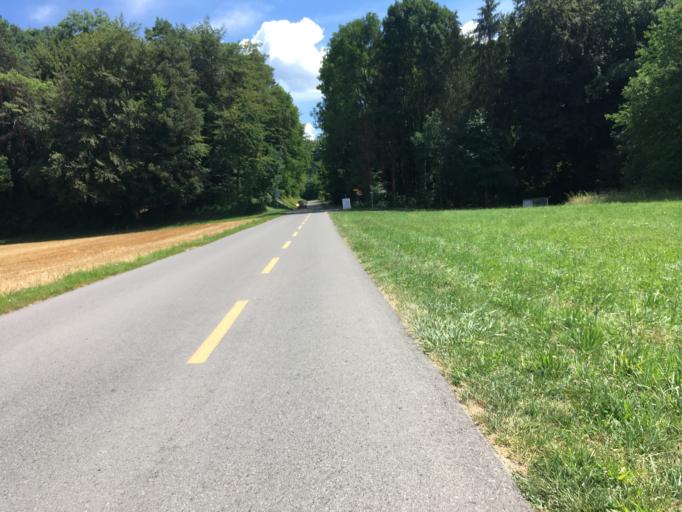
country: CH
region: Vaud
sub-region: Broye-Vully District
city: Payerne
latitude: 46.9012
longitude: 6.9285
